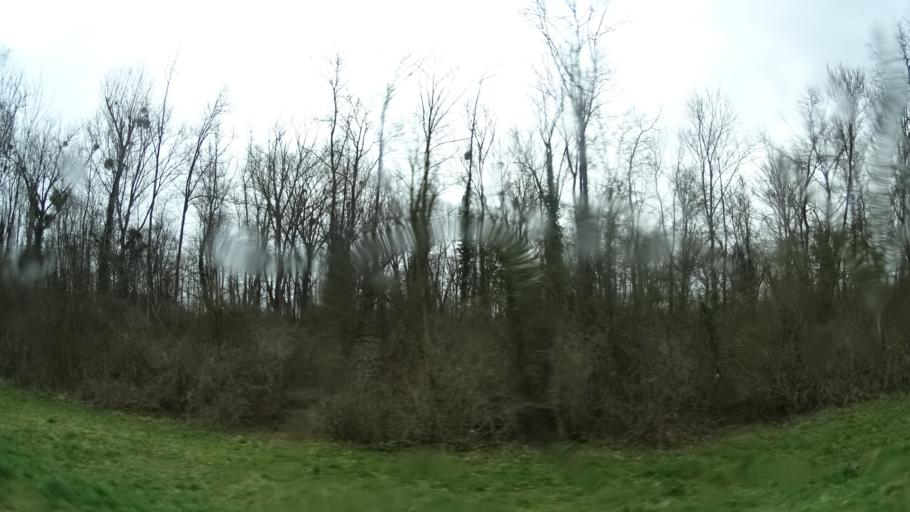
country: DE
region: Hesse
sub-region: Regierungsbezirk Darmstadt
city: Stockstadt am Rhein
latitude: 49.8335
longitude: 8.4202
